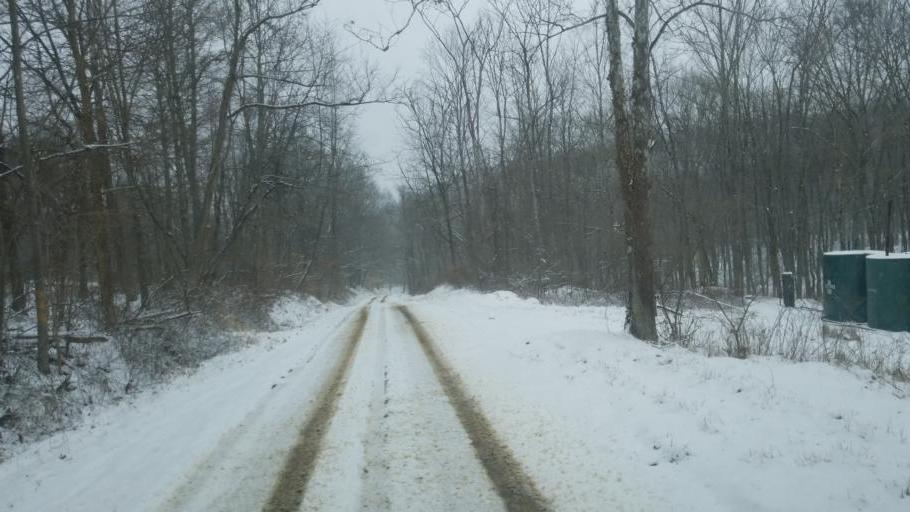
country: US
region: Ohio
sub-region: Knox County
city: Oak Hill
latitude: 40.4430
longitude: -82.1751
